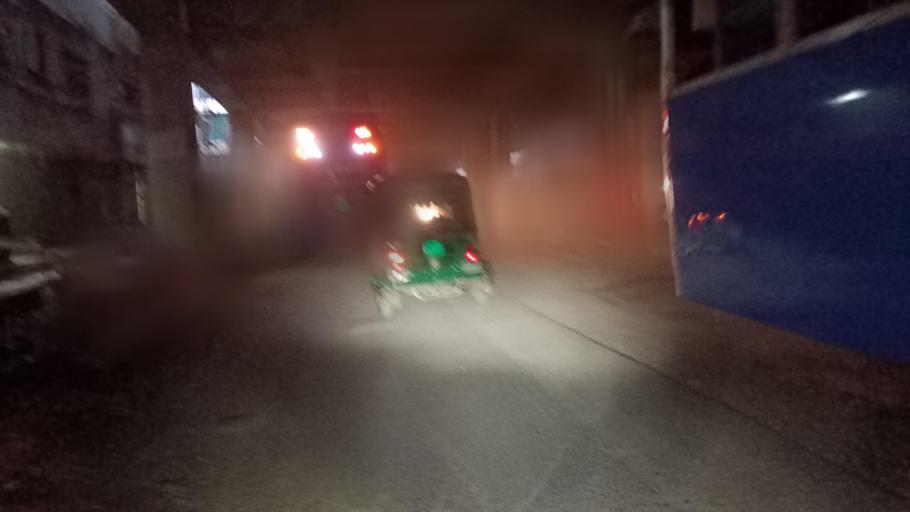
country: BD
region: Dhaka
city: Azimpur
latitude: 23.7915
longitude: 90.3751
